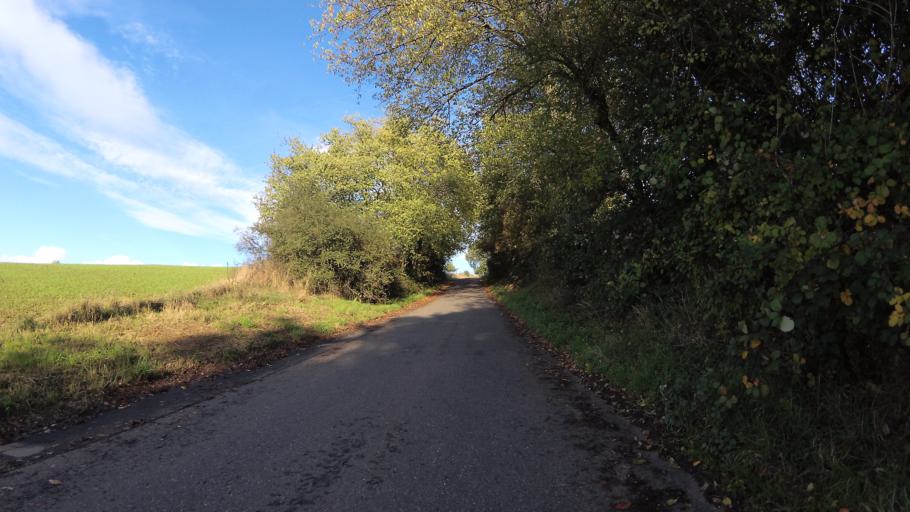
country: DE
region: Saarland
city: Marpingen
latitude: 49.4701
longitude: 7.0790
